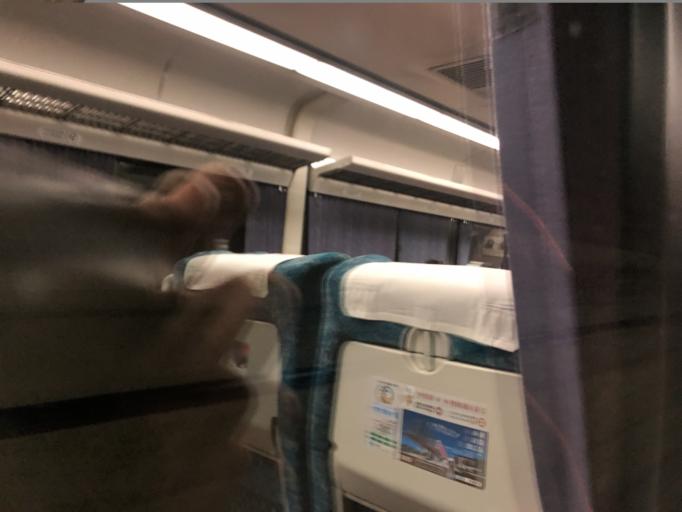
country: JP
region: Kochi
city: Nakamura
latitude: 33.1263
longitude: 133.1169
